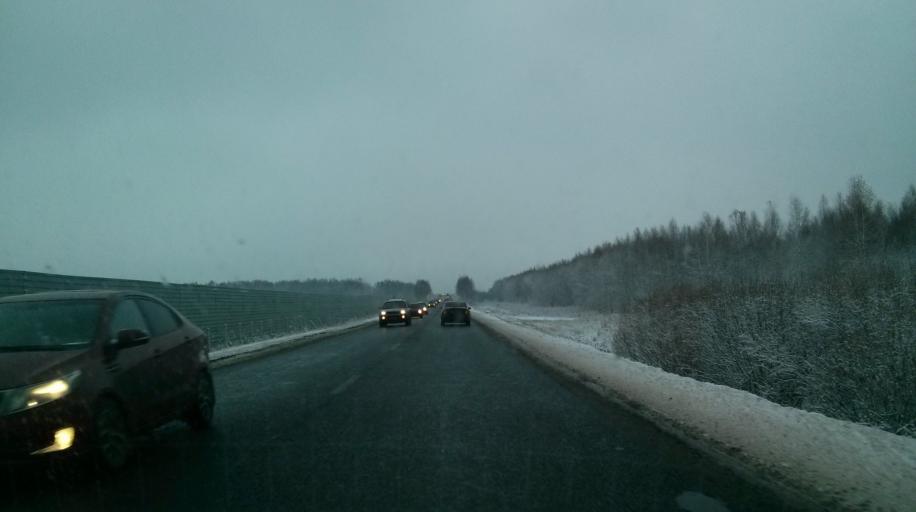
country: RU
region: Nizjnij Novgorod
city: Bogorodsk
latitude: 56.1201
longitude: 43.5951
